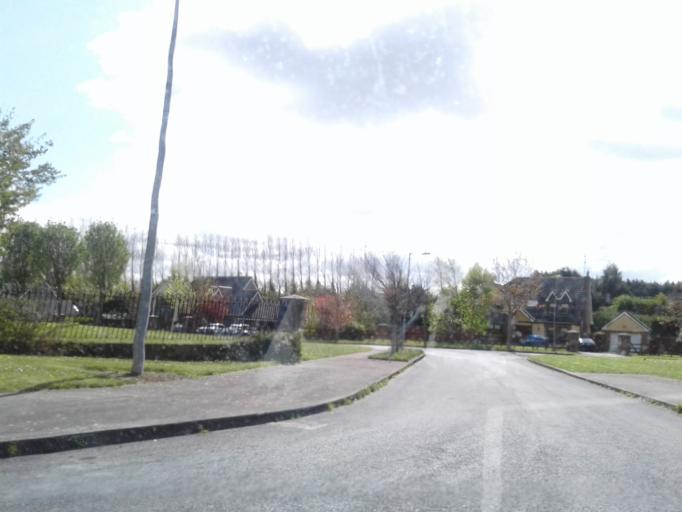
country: IE
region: Leinster
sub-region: Fingal County
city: Swords
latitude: 53.4881
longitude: -6.3047
